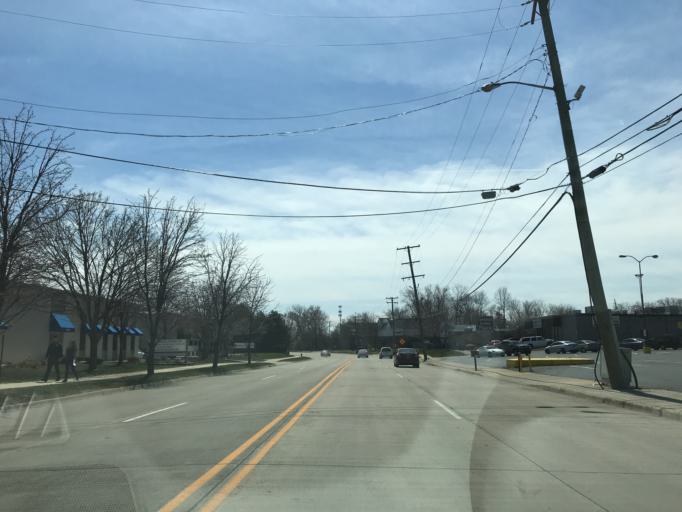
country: US
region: Michigan
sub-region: Washtenaw County
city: Ann Arbor
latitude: 42.2594
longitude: -83.7373
